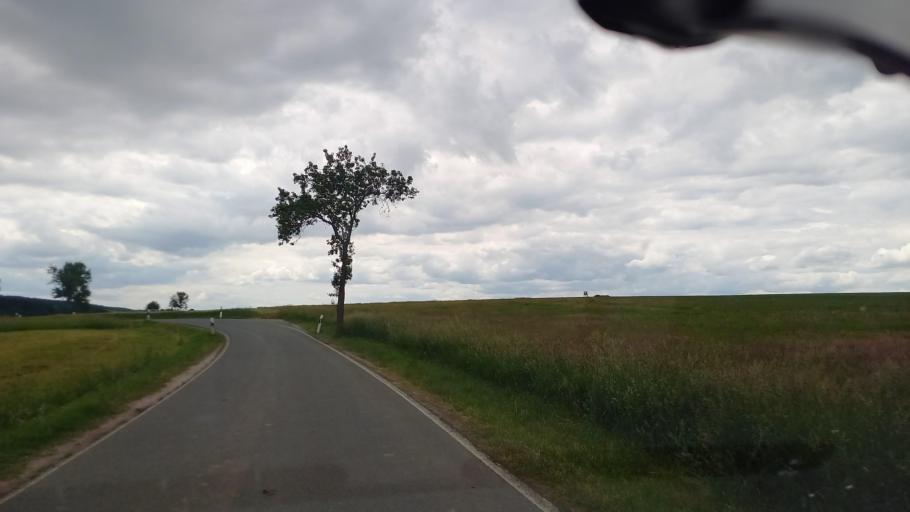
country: DE
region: Saxony
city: Waldkirchen
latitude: 50.6307
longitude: 12.4091
